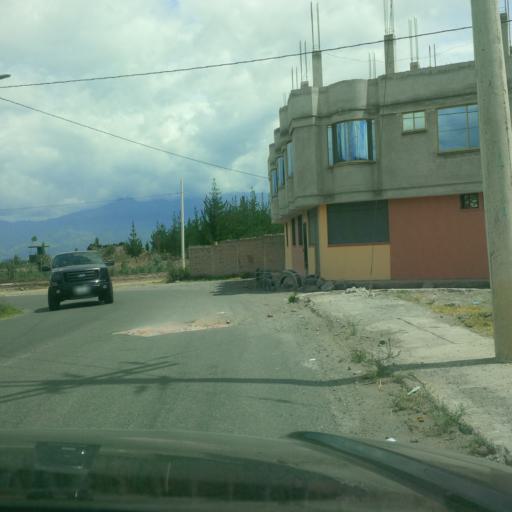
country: EC
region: Chimborazo
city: Riobamba
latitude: -1.6435
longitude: -78.6636
